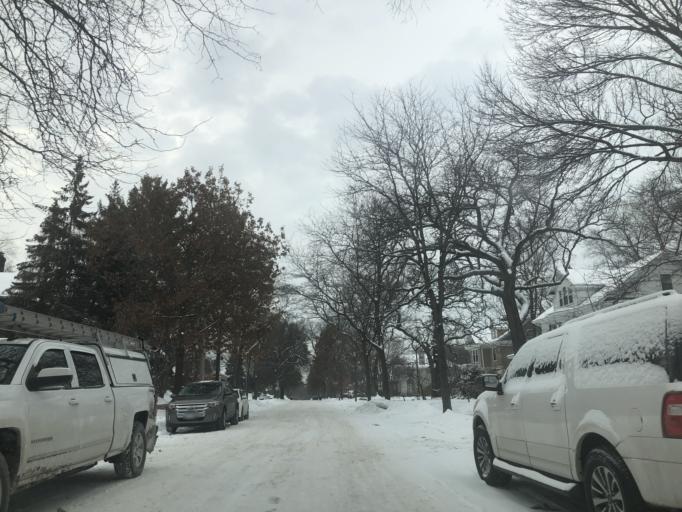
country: US
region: Minnesota
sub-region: Hennepin County
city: Richfield
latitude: 44.9170
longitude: -93.2960
